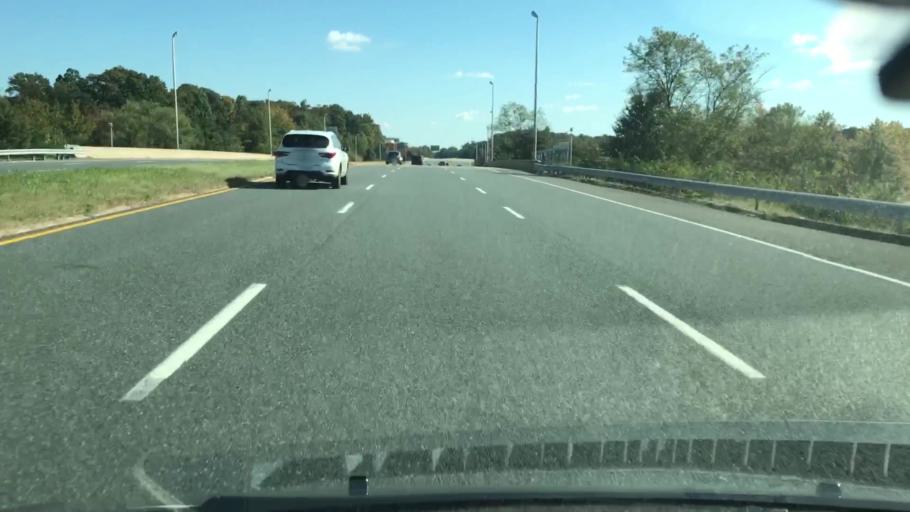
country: US
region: Virginia
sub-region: Fairfax County
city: Springfield
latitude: 38.7693
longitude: -77.1721
